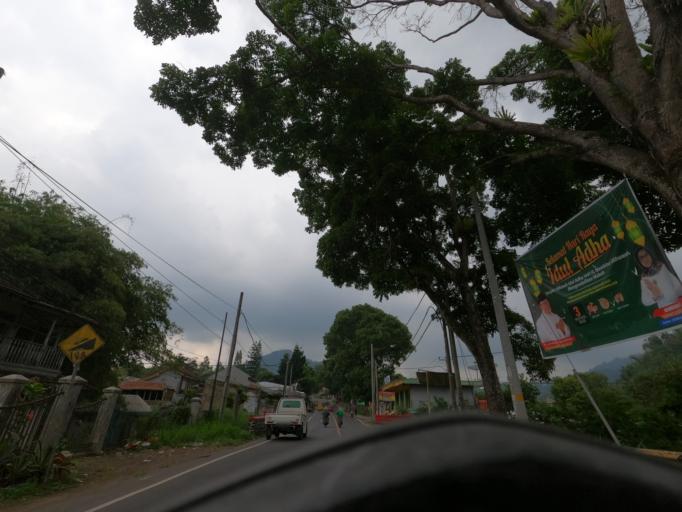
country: ID
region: West Java
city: Sukabumi
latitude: -6.7773
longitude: 107.0634
